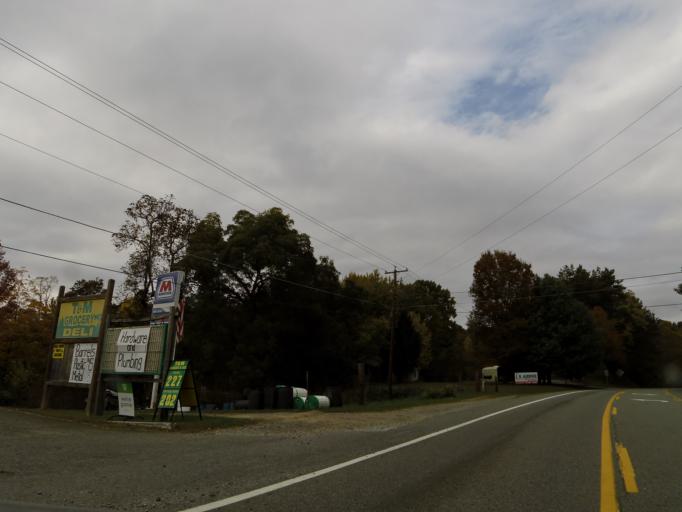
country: US
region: Virginia
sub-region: Carroll County
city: Cana
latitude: 36.6084
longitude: -80.6875
